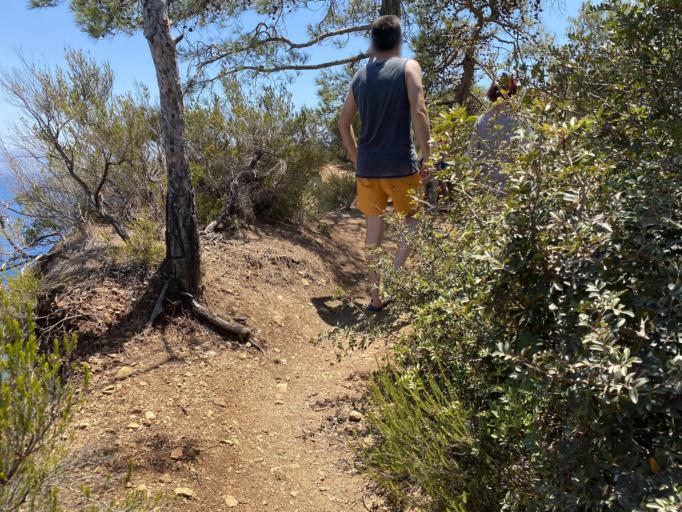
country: TR
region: Mugla
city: Goecek
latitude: 36.7068
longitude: 28.9347
